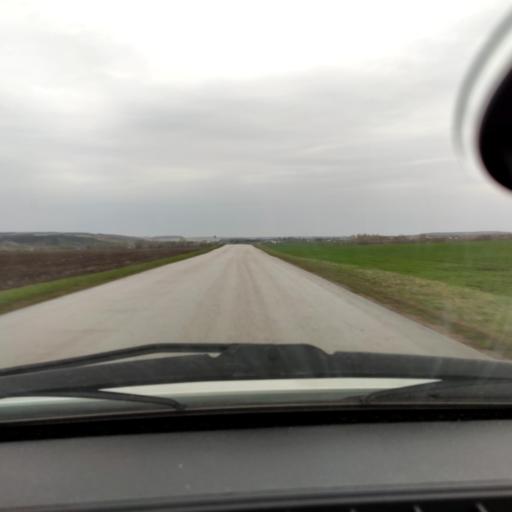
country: RU
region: Bashkortostan
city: Tolbazy
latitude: 54.1710
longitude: 55.9276
